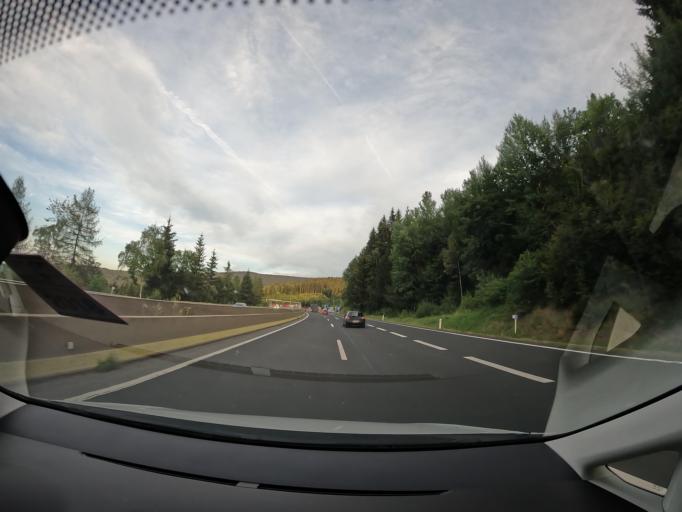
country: AT
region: Styria
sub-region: Politischer Bezirk Voitsberg
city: Edelschrott
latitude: 46.9878
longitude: 15.1046
